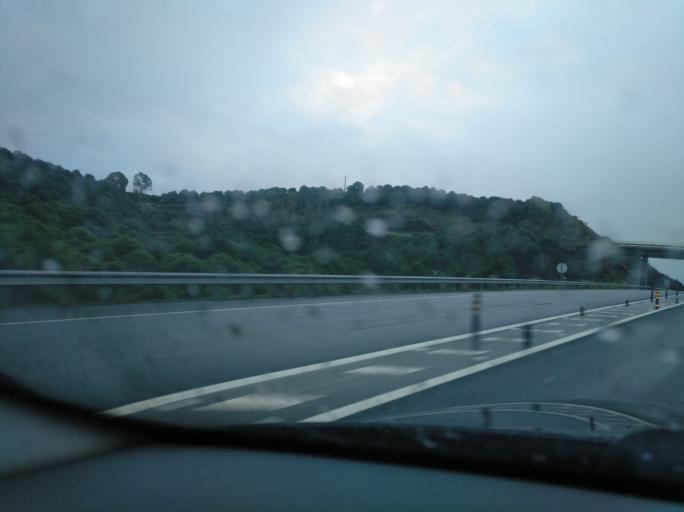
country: PT
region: Faro
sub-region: Castro Marim
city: Castro Marim
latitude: 37.3393
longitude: -7.5021
